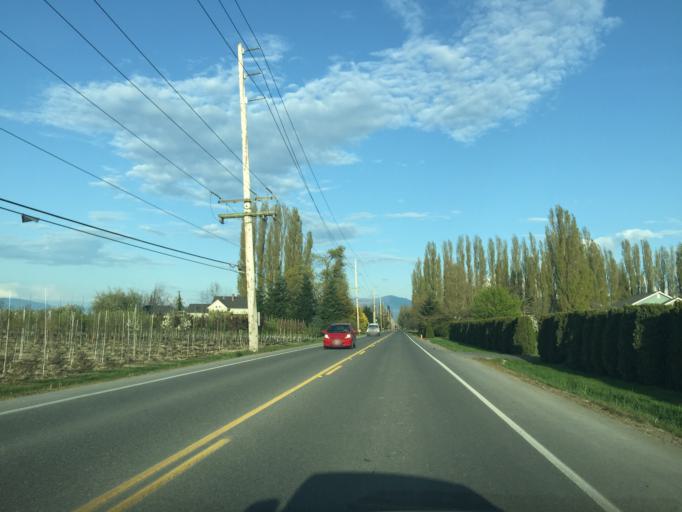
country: US
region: Washington
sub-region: Skagit County
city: Mount Vernon
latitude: 48.4208
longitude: -122.4218
